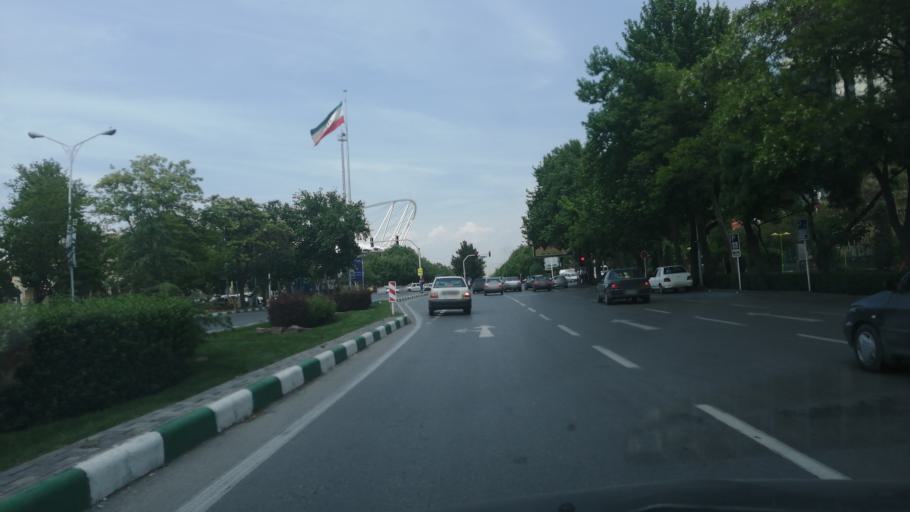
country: IR
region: Razavi Khorasan
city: Mashhad
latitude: 36.3234
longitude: 59.5692
